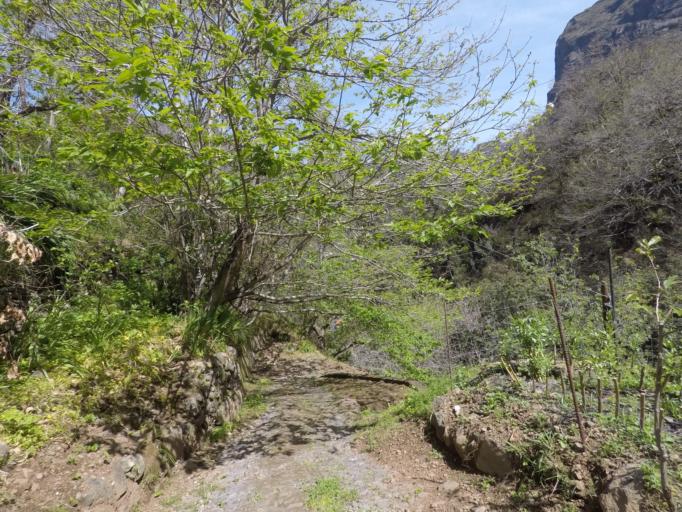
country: PT
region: Madeira
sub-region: Camara de Lobos
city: Curral das Freiras
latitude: 32.7252
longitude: -16.9646
